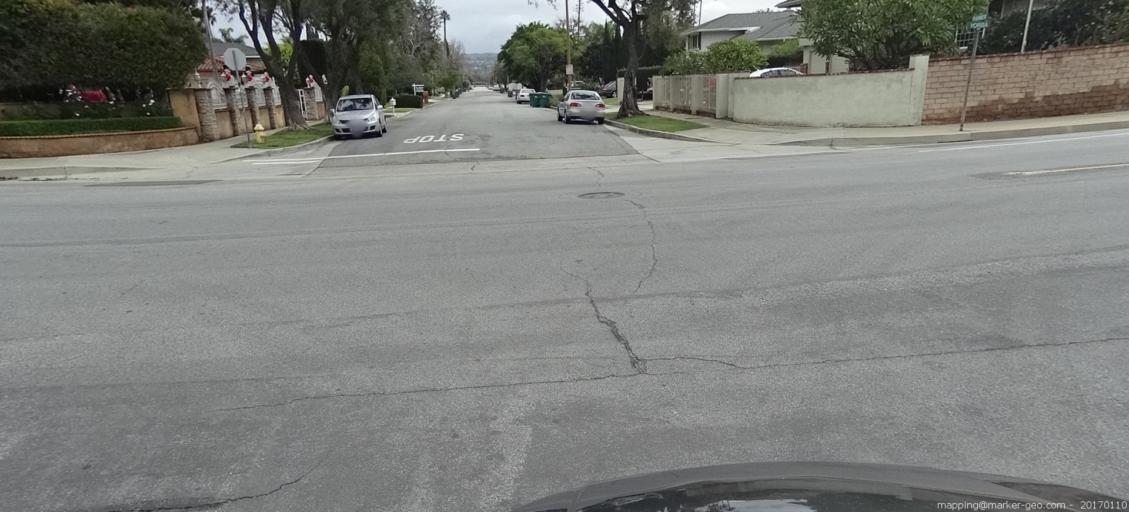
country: US
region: California
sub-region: Orange County
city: Tustin
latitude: 33.7703
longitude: -117.8272
